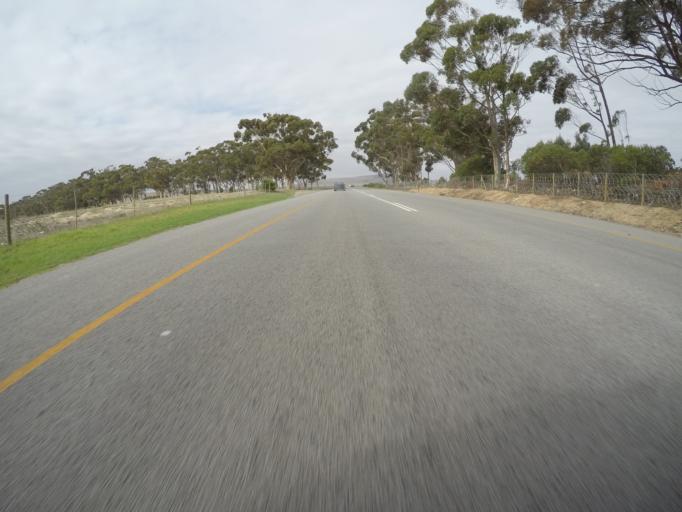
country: ZA
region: Western Cape
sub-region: City of Cape Town
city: Sunset Beach
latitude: -33.7222
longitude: 18.5059
